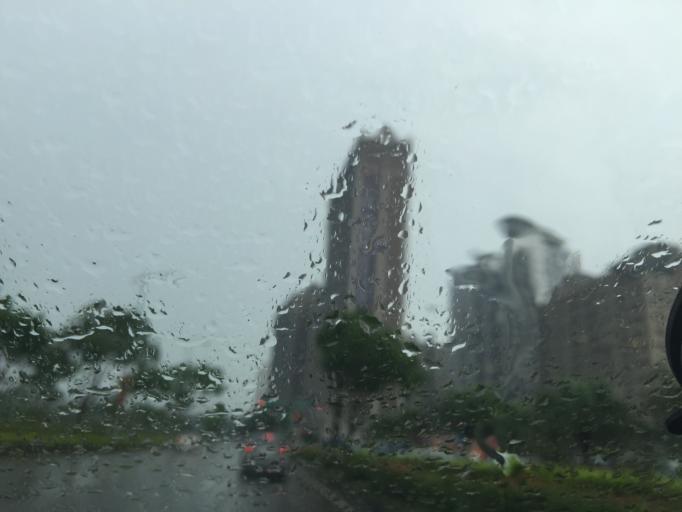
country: TW
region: Taiwan
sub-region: Hsinchu
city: Zhubei
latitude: 24.8119
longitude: 121.0364
